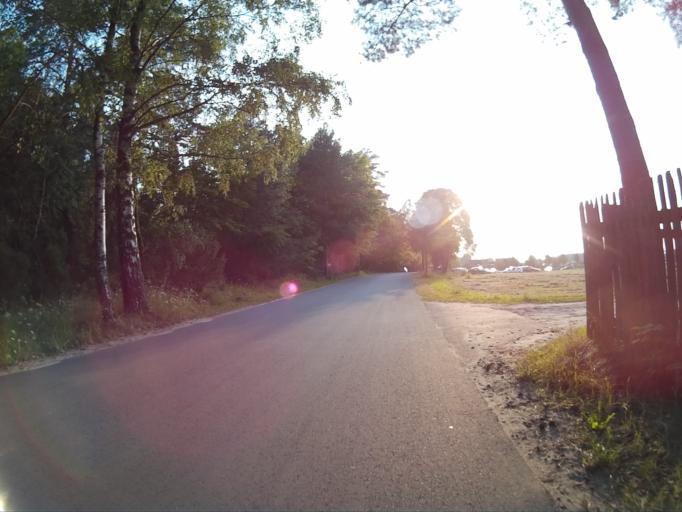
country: PL
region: Pomeranian Voivodeship
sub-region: Powiat chojnicki
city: Czersk
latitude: 53.7227
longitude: 17.9147
